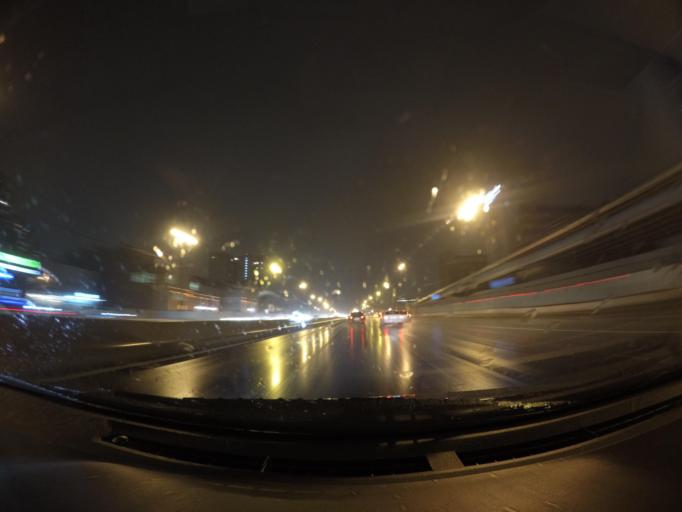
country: RU
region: Moskovskaya
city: Kur'yanovo
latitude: 55.6413
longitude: 37.6835
